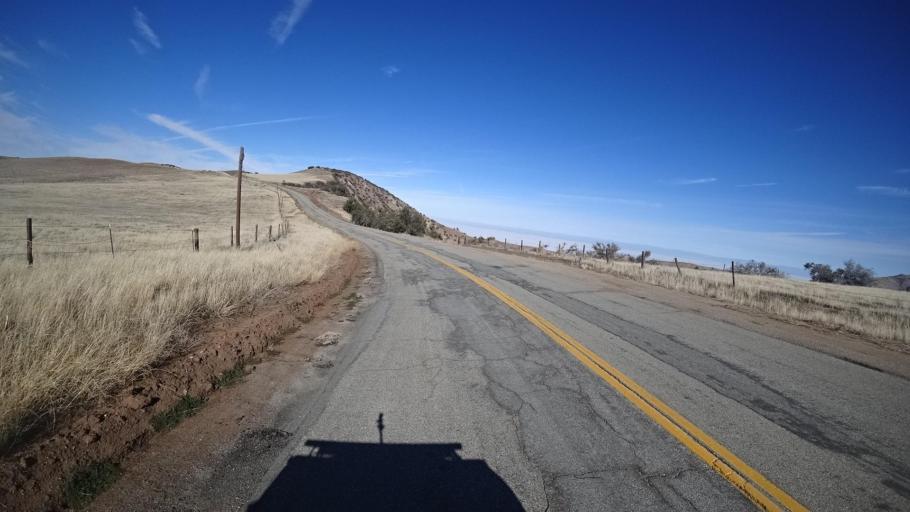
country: US
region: California
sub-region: Kern County
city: Maricopa
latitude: 34.8842
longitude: -119.3533
